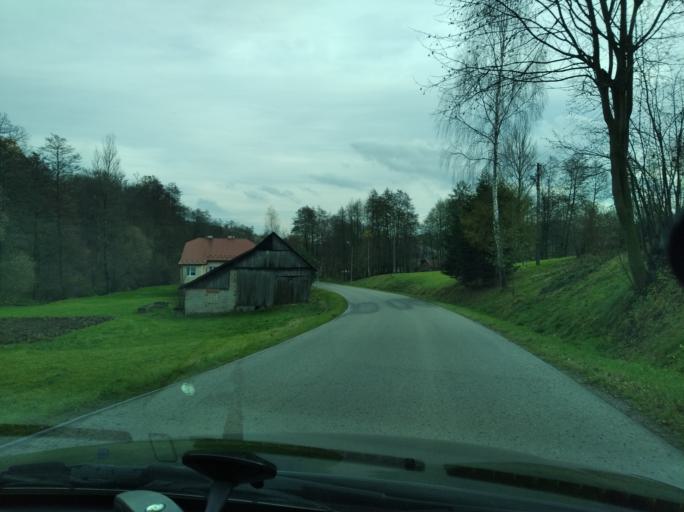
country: PL
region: Subcarpathian Voivodeship
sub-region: Powiat ropczycko-sedziszowski
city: Zagorzyce
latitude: 49.9521
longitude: 21.7245
